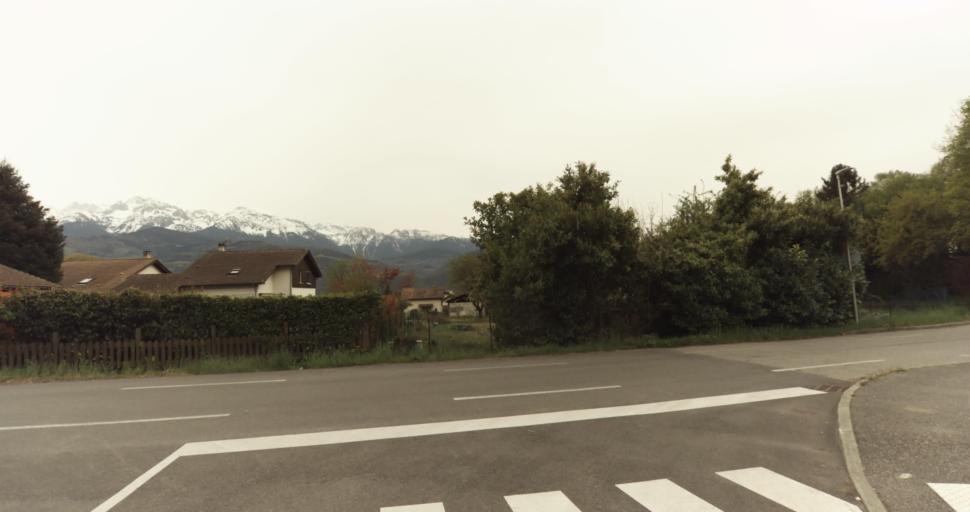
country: FR
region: Rhone-Alpes
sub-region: Departement de l'Isere
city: Saint-Ismier
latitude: 45.2314
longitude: 5.8193
